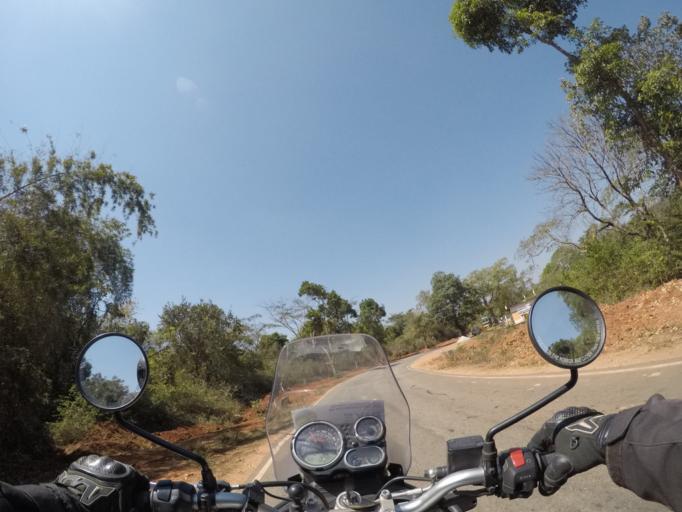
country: IN
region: Karnataka
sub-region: Hassan
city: Sakleshpur
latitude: 12.9387
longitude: 75.7563
